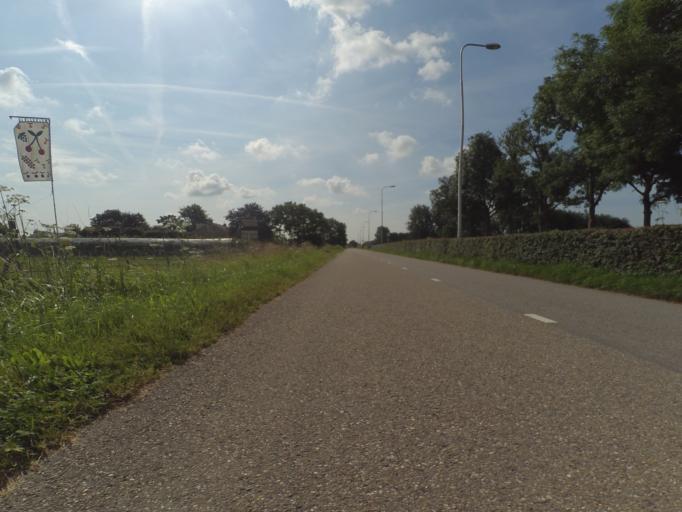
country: NL
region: Utrecht
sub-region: Gemeente Bunnik
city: Bunnik
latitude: 52.0410
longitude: 5.2326
